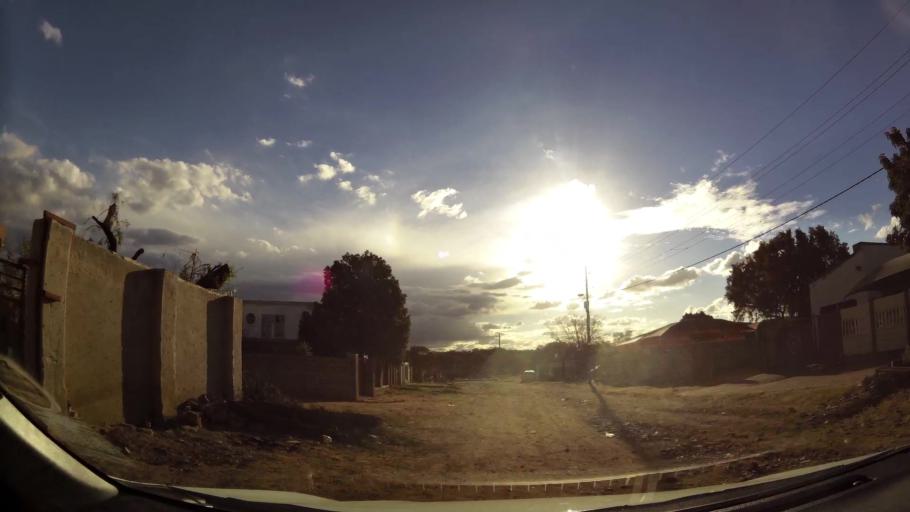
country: ZA
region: Limpopo
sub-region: Capricorn District Municipality
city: Polokwane
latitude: -23.9113
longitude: 29.4247
